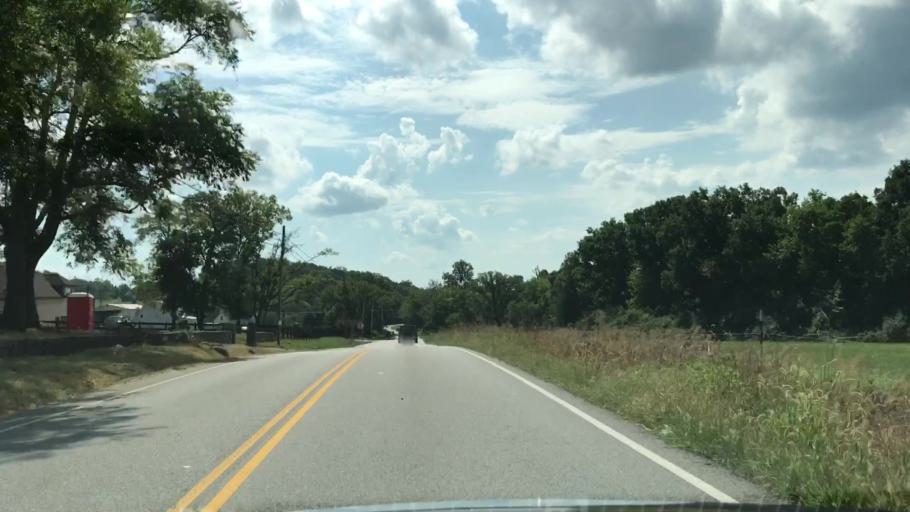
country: US
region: Tennessee
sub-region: Trousdale County
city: Hartsville
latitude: 36.4114
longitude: -86.1775
